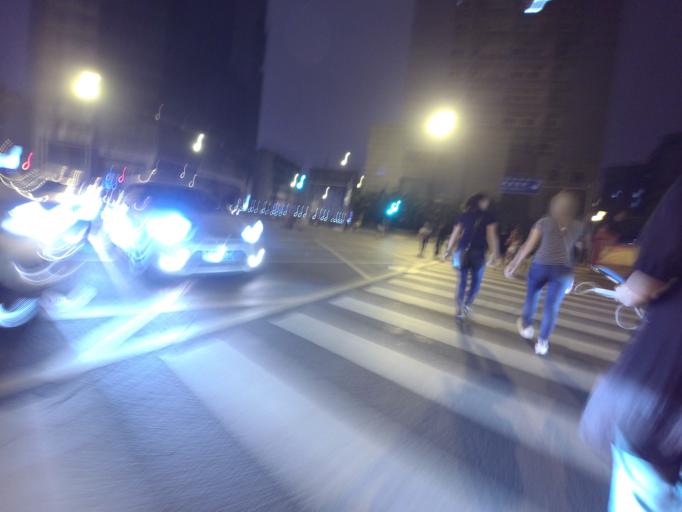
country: CN
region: Sichuan
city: Chengdu
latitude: 30.6693
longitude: 104.0578
